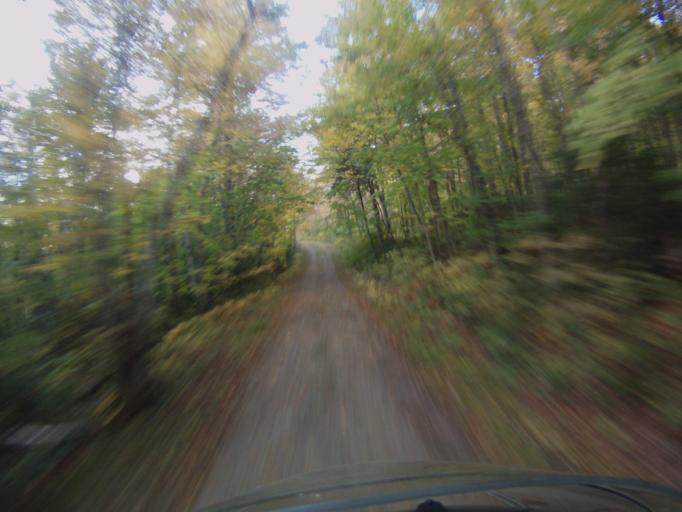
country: US
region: Vermont
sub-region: Addison County
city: Bristol
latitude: 44.1003
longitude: -72.9539
